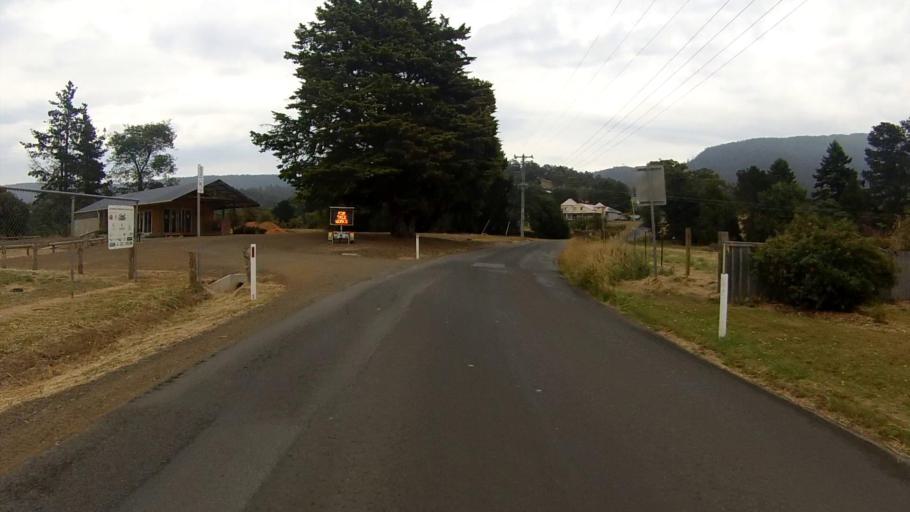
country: AU
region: Tasmania
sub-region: Kingborough
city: Kettering
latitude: -43.1603
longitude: 147.2356
